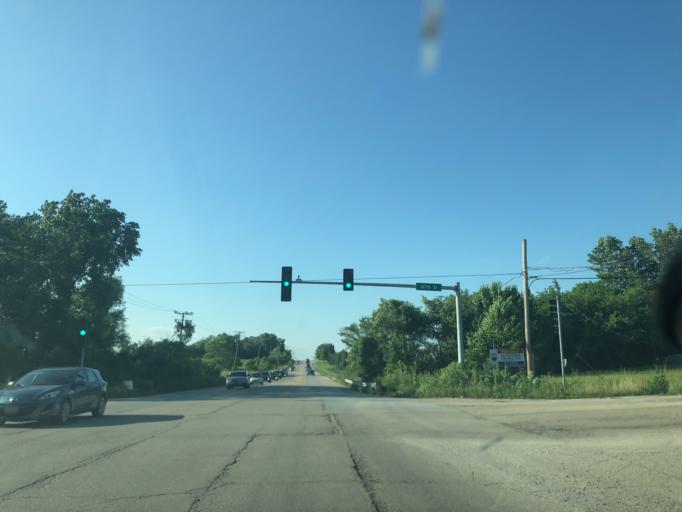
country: US
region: Illinois
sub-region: Cook County
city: Orland Hills
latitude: 41.5860
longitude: -87.8910
